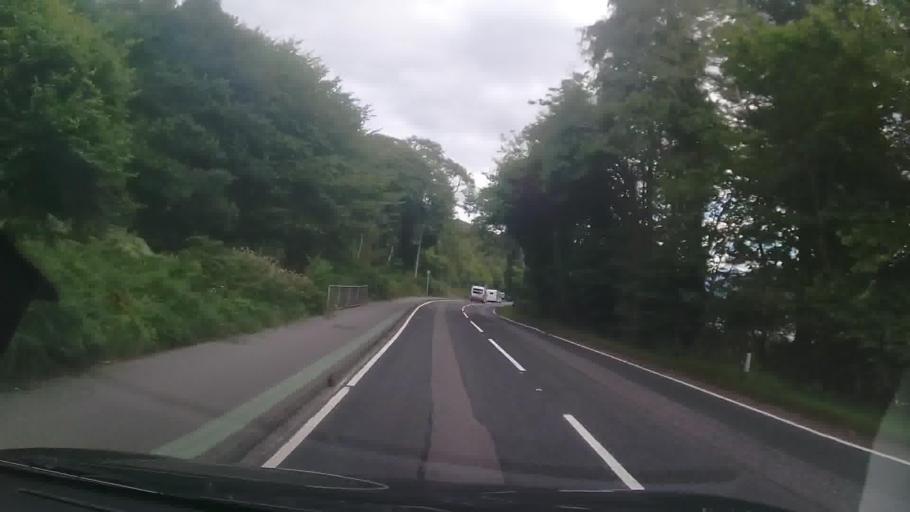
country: GB
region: Scotland
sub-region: Highland
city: Fort William
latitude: 56.7028
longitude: -5.2120
